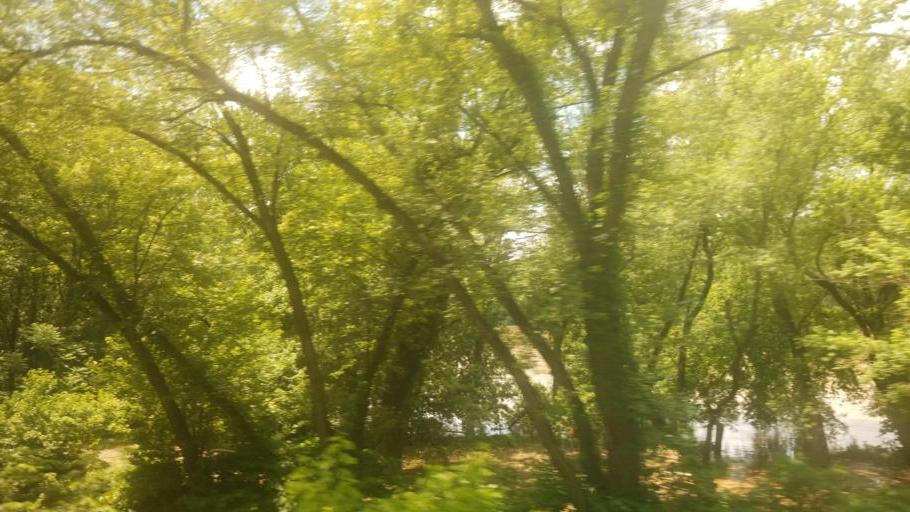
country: US
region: Maryland
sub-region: Frederick County
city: Point of Rocks
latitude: 39.2988
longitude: -77.5568
